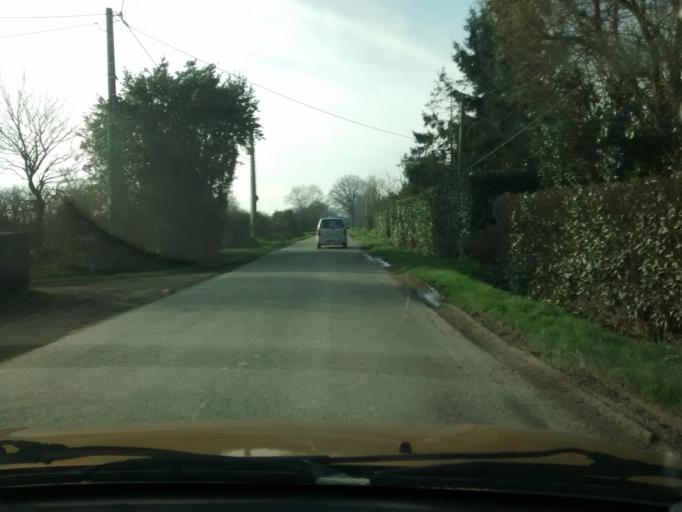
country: FR
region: Pays de la Loire
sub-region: Departement de la Loire-Atlantique
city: Notre-Dame-des-Landes
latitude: 47.3570
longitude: -1.7291
